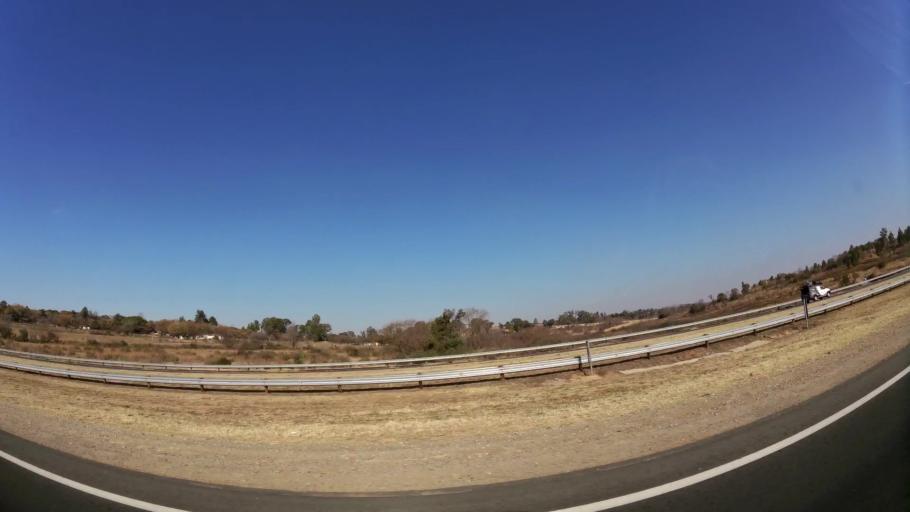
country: ZA
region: Gauteng
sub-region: West Rand District Municipality
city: Muldersdriseloop
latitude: -25.9984
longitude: 27.9052
